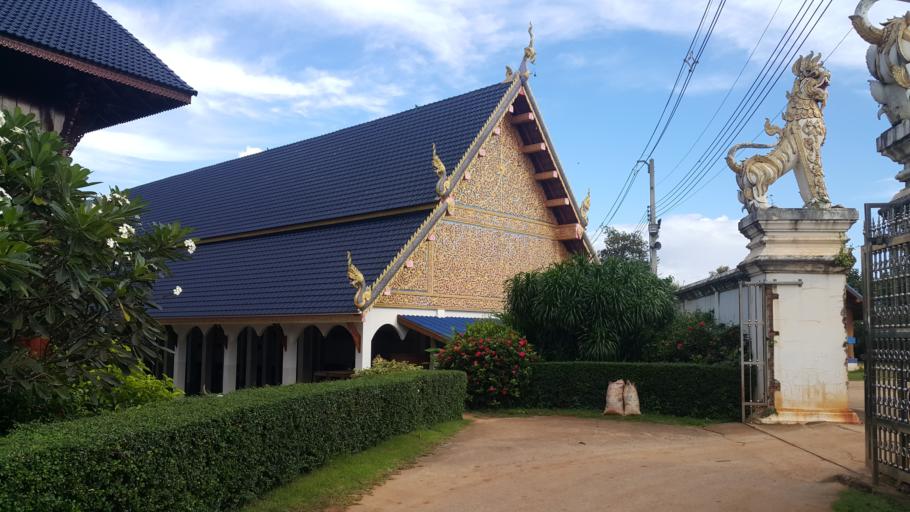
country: TH
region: Chiang Mai
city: Mae Taeng
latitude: 19.1562
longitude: 98.9778
